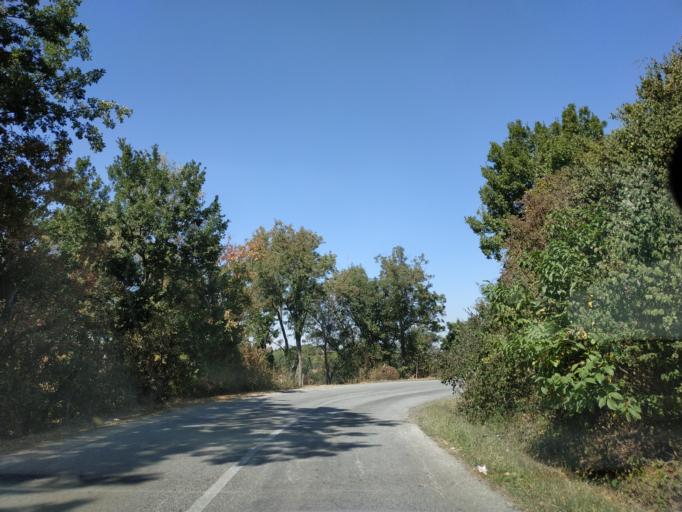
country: RS
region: Central Serbia
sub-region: Sumadijski Okrug
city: Topola
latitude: 44.2604
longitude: 20.6728
